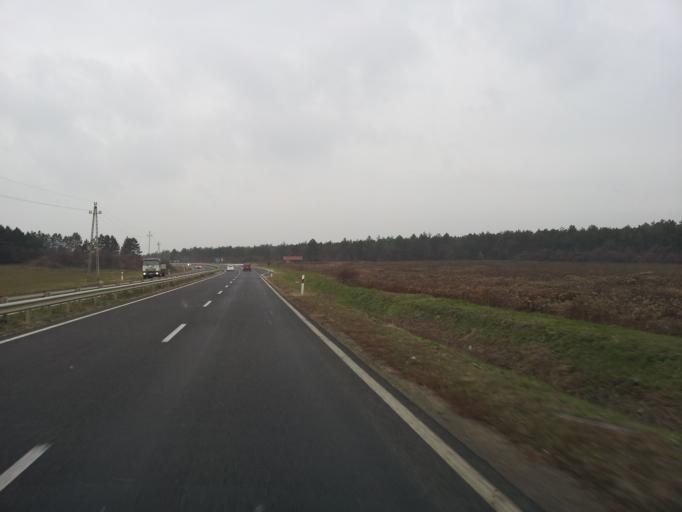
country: HU
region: Veszprem
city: Nemesvamos
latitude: 47.1174
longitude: 17.8420
